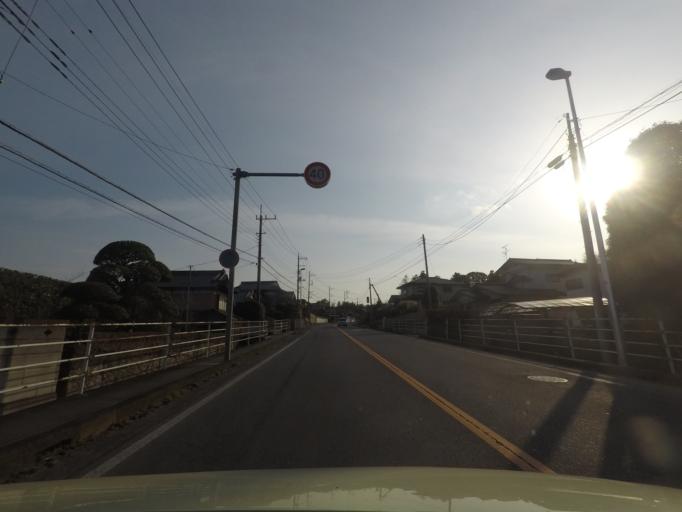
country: JP
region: Ibaraki
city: Okunoya
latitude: 36.2858
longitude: 140.4215
